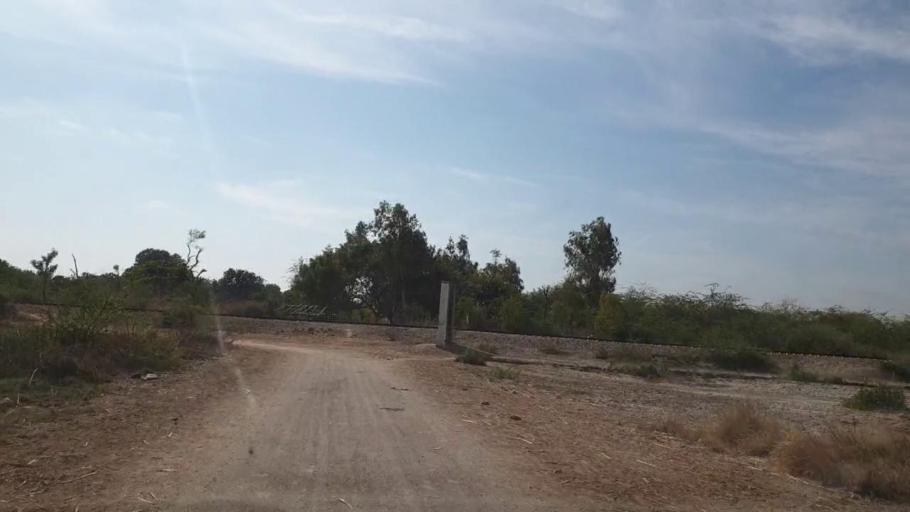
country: PK
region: Sindh
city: Mirpur Khas
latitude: 25.5224
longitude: 69.1457
